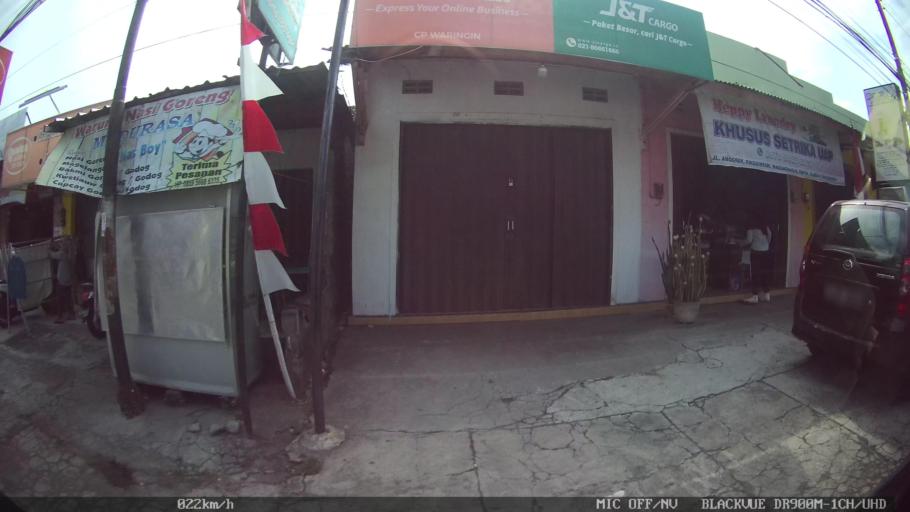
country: ID
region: Daerah Istimewa Yogyakarta
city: Depok
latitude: -7.7758
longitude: 110.4355
